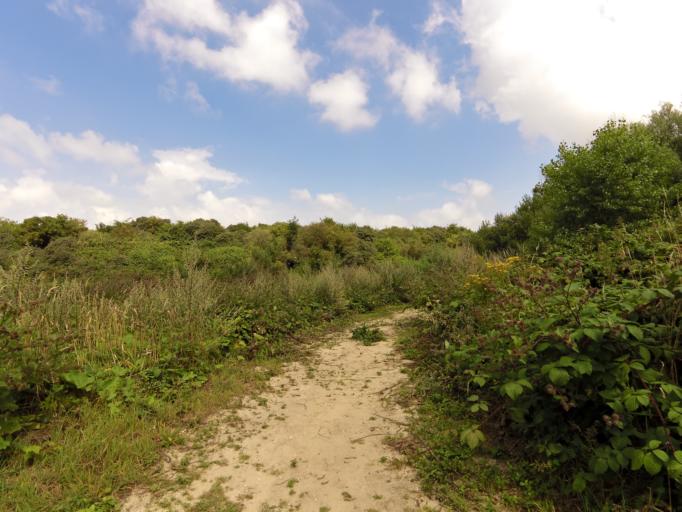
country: NL
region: Zeeland
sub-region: Gemeente Sluis
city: Sluis
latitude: 51.3602
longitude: 3.3459
